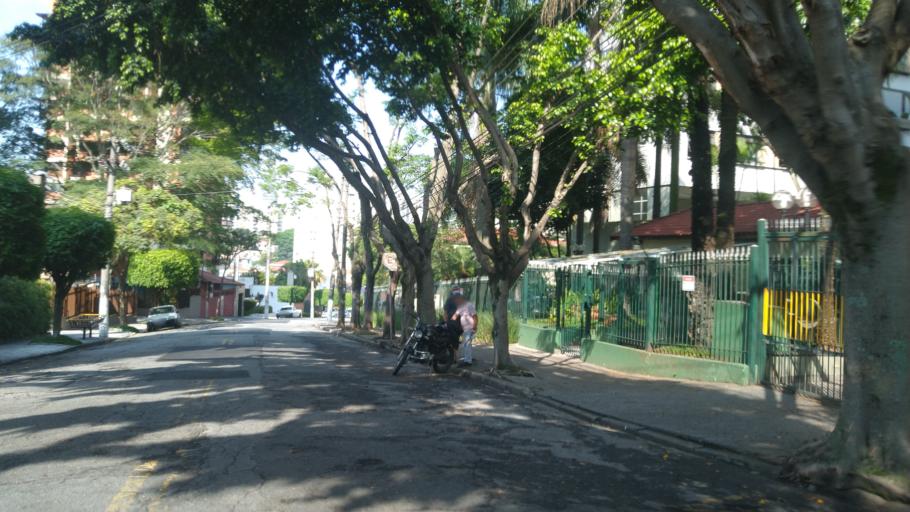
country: BR
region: Sao Paulo
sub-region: Sao Paulo
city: Sao Paulo
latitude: -23.4855
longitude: -46.6173
